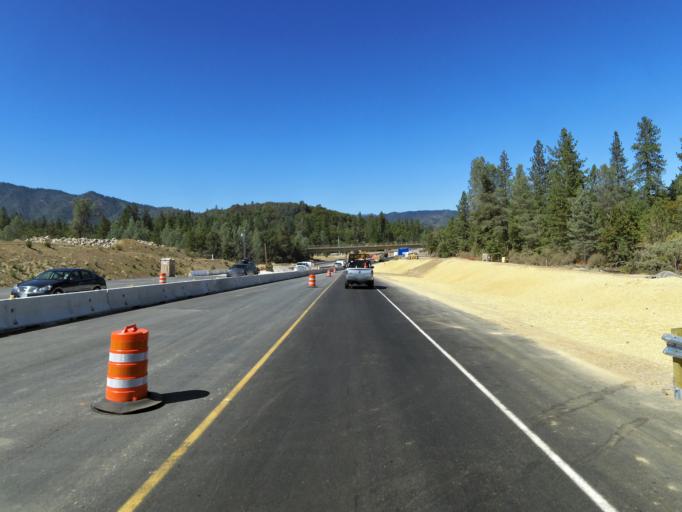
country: US
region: California
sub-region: Shasta County
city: Central Valley (historical)
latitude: 40.8836
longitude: -122.3826
